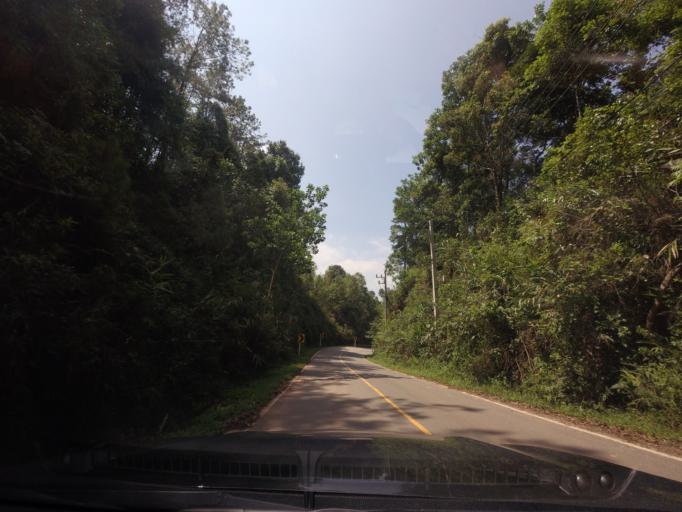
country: TH
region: Loei
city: Na Haeo
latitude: 17.4680
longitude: 100.9245
